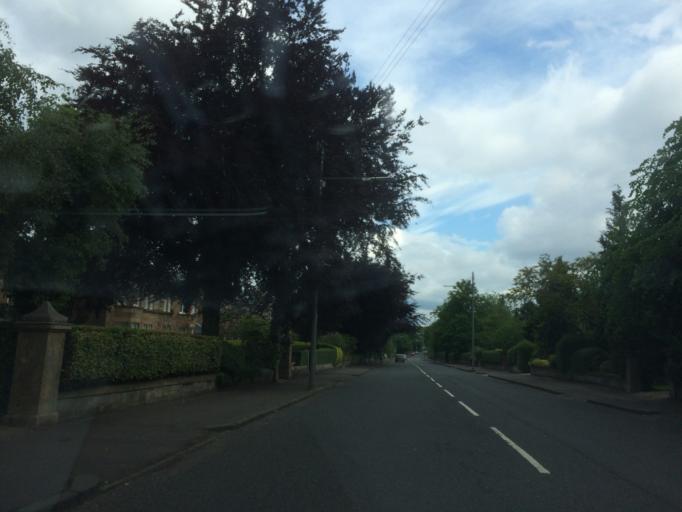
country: GB
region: Scotland
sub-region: East Renfrewshire
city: Giffnock
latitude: 55.8160
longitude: -4.2781
